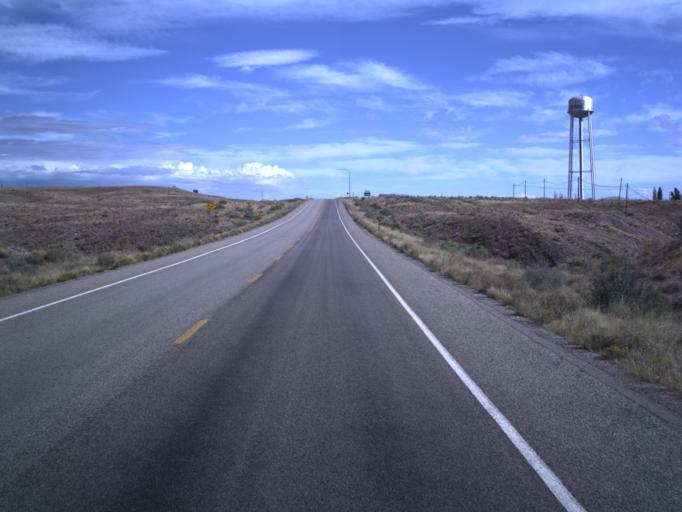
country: US
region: Colorado
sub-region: Montezuma County
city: Towaoc
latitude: 37.2015
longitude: -109.1560
